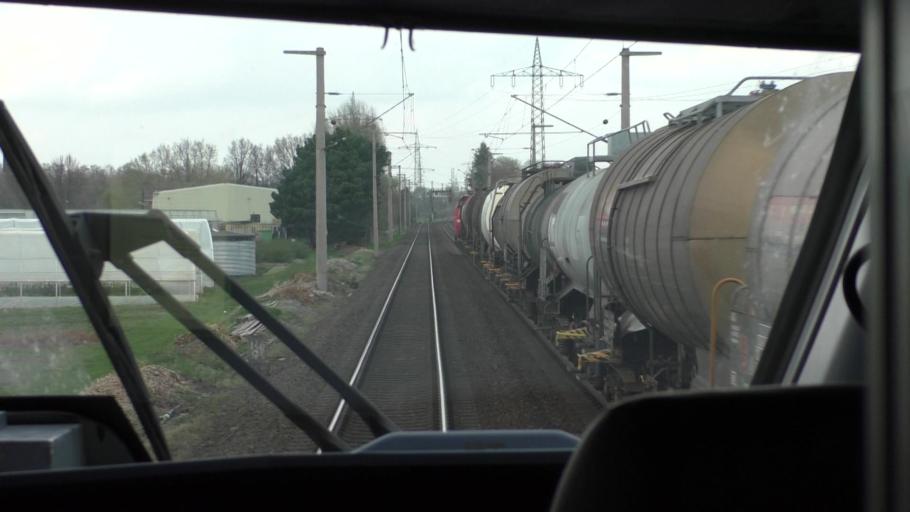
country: DE
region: North Rhine-Westphalia
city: Bruhl
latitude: 50.8612
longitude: 6.9087
